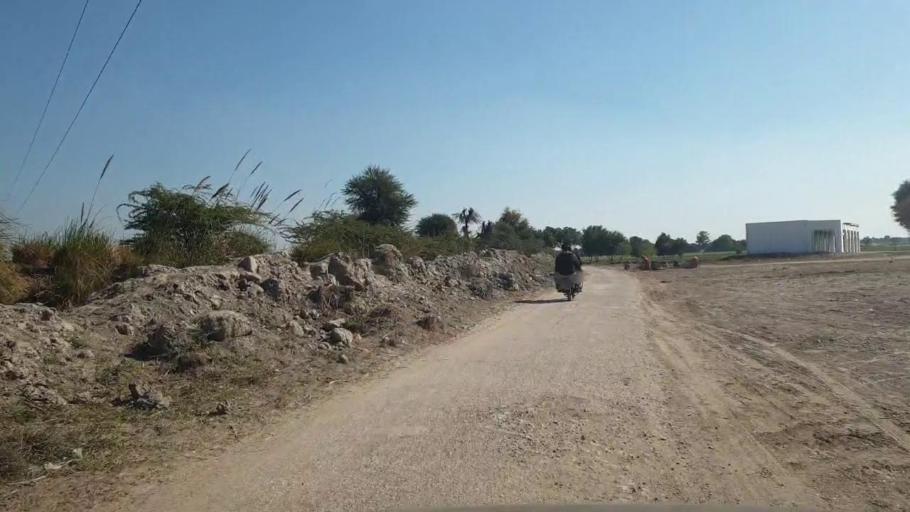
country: PK
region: Sindh
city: Shahpur Chakar
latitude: 26.1477
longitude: 68.6439
